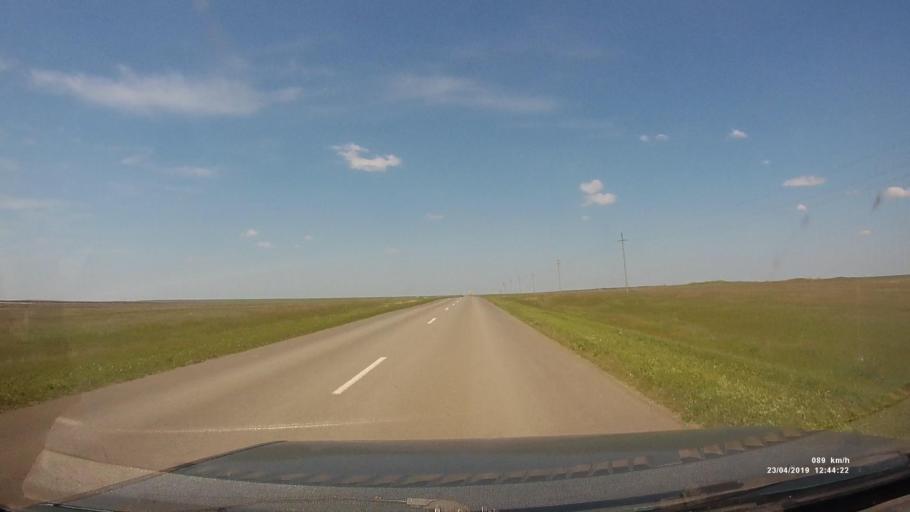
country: RU
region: Kalmykiya
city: Yashalta
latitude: 46.4760
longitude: 42.6478
